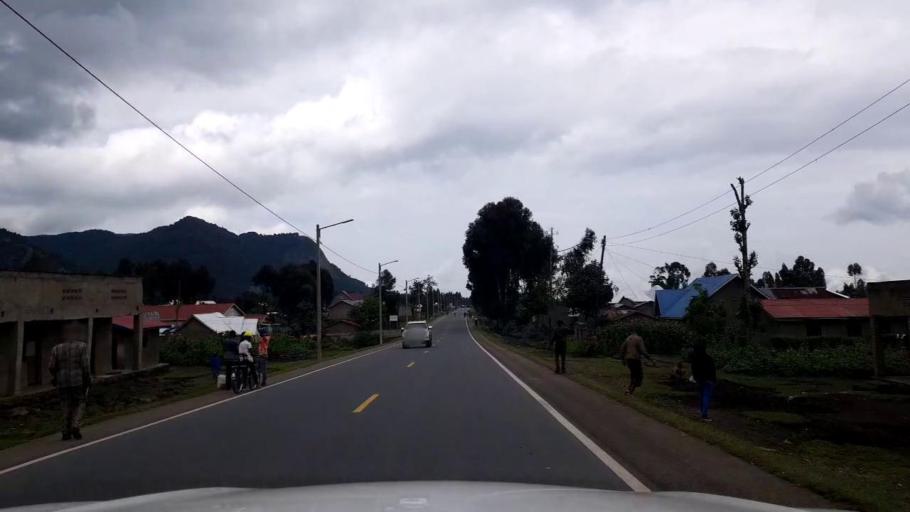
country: RW
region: Western Province
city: Gisenyi
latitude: -1.6344
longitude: 29.4106
